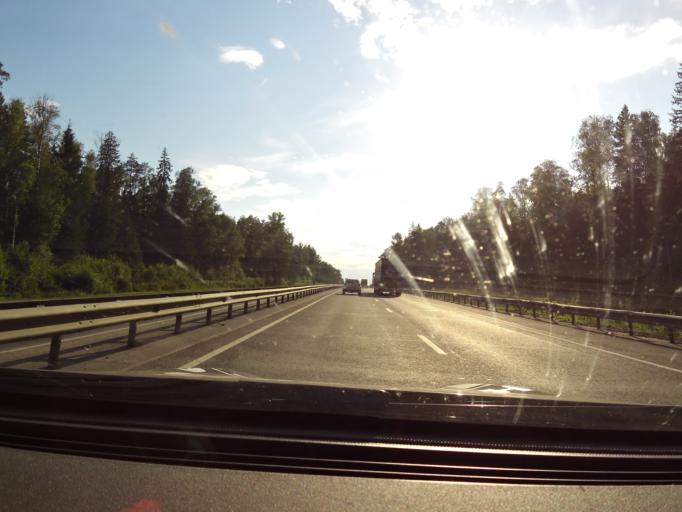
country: RU
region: Vladimir
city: Melekhovo
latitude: 56.2142
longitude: 41.3659
